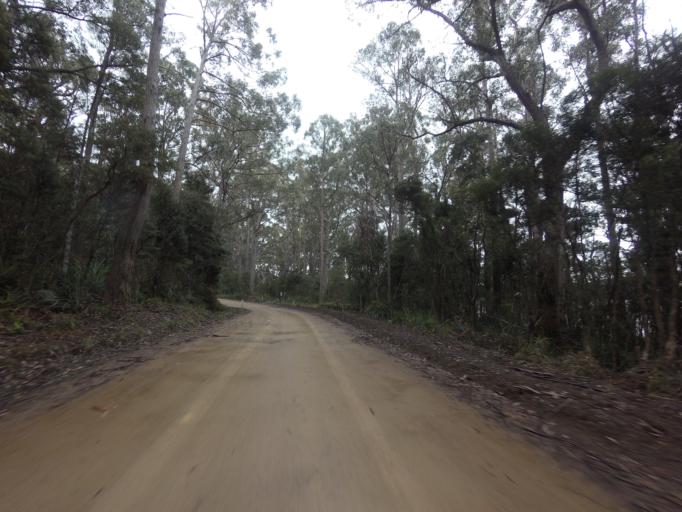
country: AU
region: Tasmania
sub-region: Huon Valley
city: Geeveston
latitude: -43.5290
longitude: 146.8957
